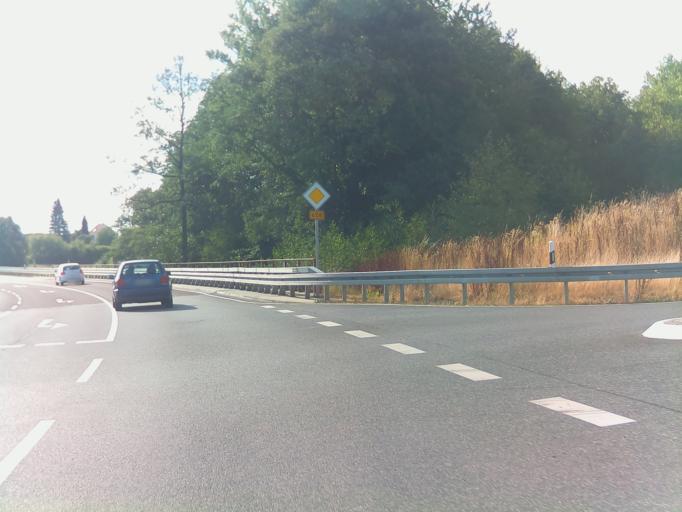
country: DE
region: Hesse
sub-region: Regierungsbezirk Kassel
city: Dipperz
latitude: 50.5353
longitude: 9.8148
